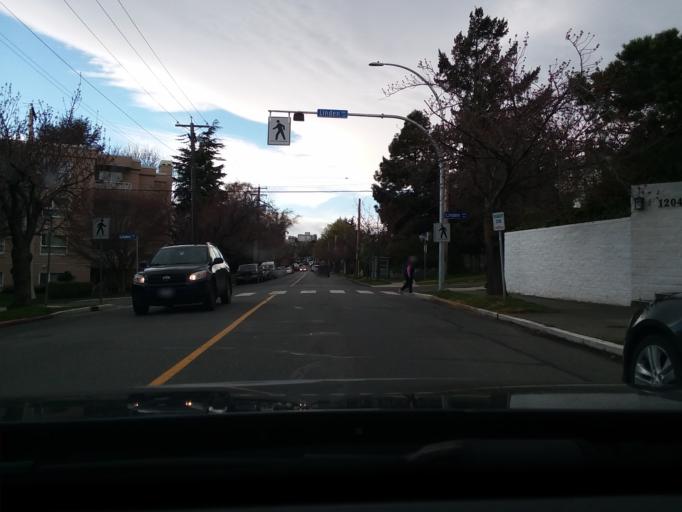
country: CA
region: British Columbia
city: Victoria
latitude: 48.4168
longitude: -123.3518
